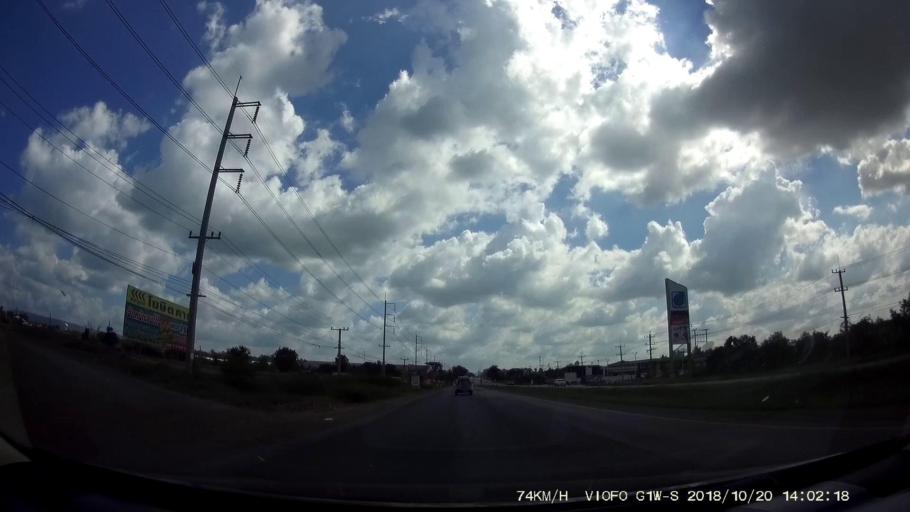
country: TH
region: Khon Kaen
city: Chum Phae
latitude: 16.4933
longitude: 102.1248
